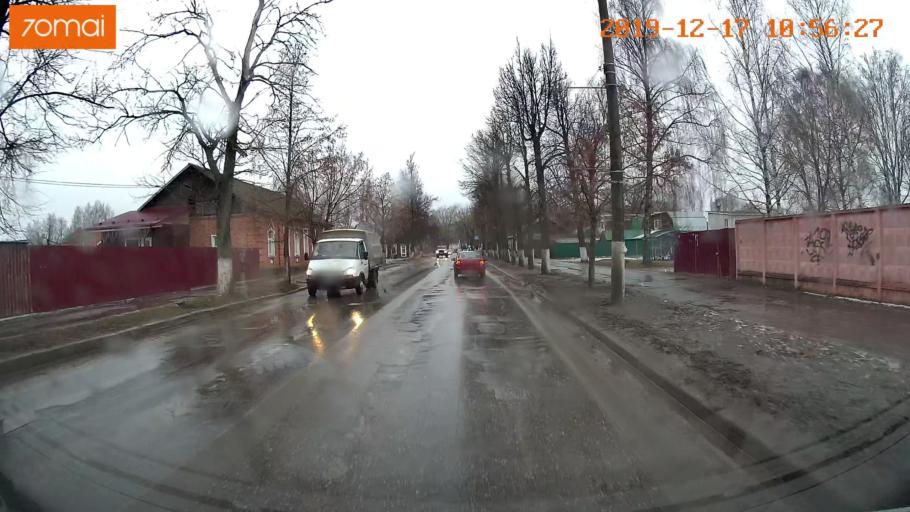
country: RU
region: Vladimir
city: Gus'-Khrustal'nyy
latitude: 55.6181
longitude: 40.6629
